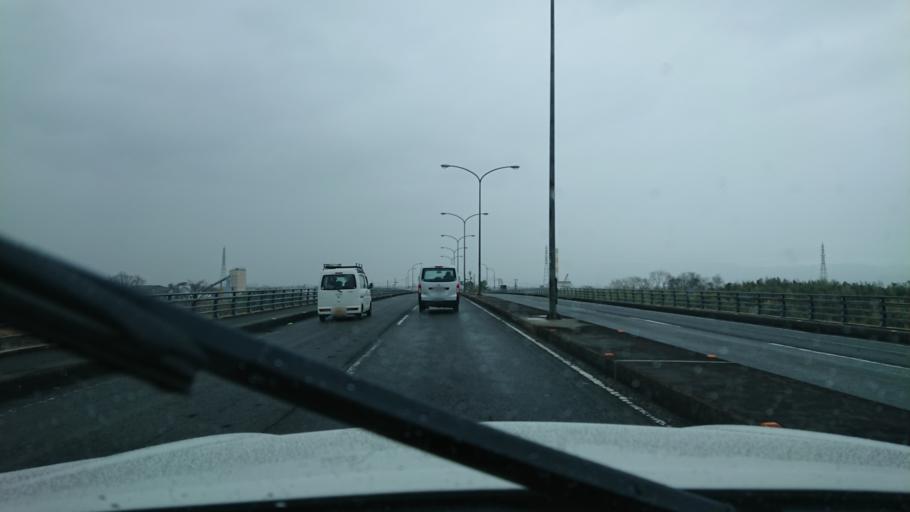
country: JP
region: Tokushima
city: Tokushima-shi
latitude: 34.0820
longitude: 134.5033
